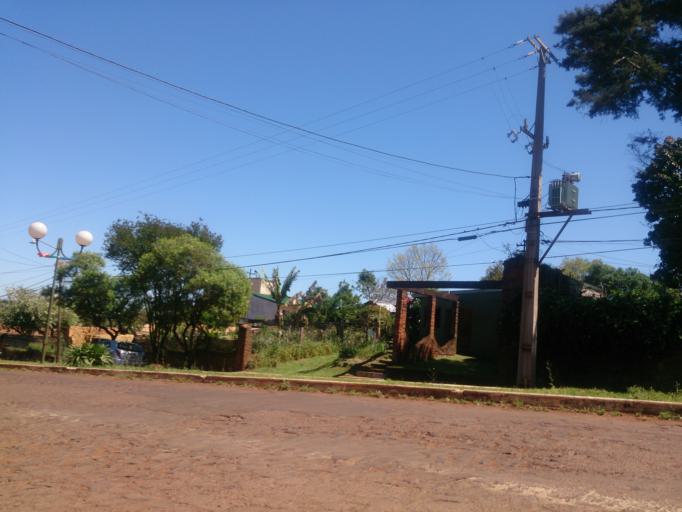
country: AR
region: Misiones
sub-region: Departamento de Obera
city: Obera
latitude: -27.4927
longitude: -55.1111
